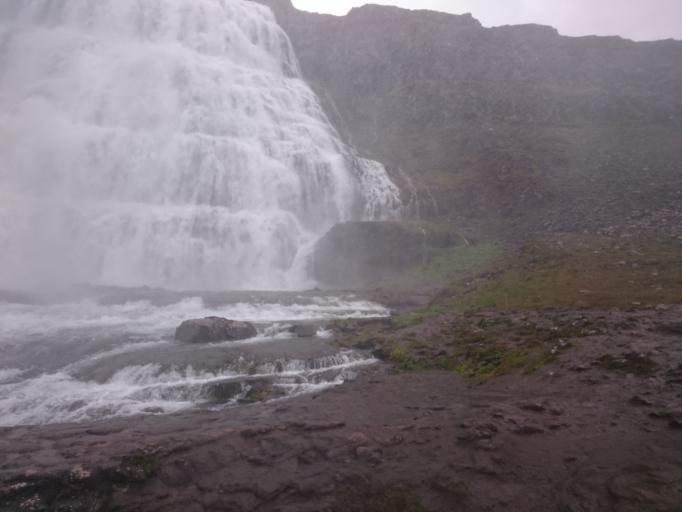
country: IS
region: Westfjords
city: Isafjoerdur
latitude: 65.7334
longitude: -23.2014
